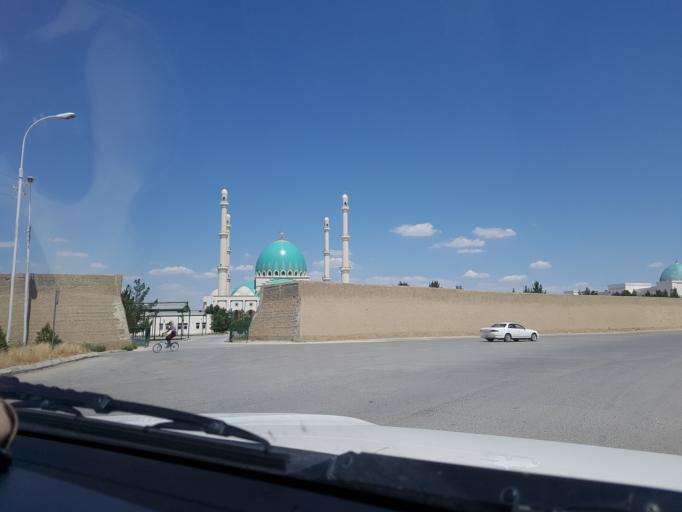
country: TM
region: Ahal
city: Abadan
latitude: 38.1612
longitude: 57.9644
